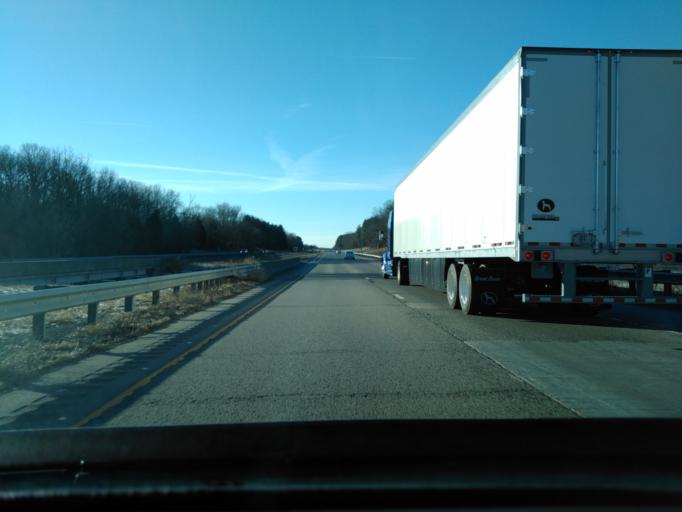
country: US
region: Illinois
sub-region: Franklin County
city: Benton
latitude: 38.0472
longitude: -88.9249
